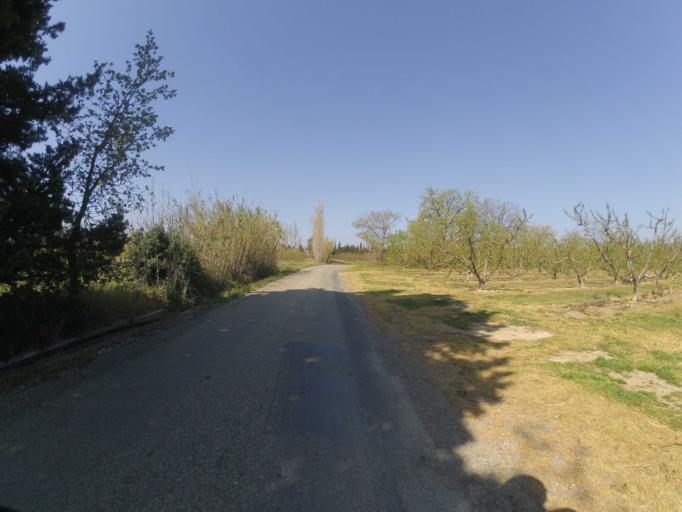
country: FR
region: Languedoc-Roussillon
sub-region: Departement des Pyrenees-Orientales
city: Pezilla-la-Riviere
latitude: 42.6755
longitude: 2.7518
